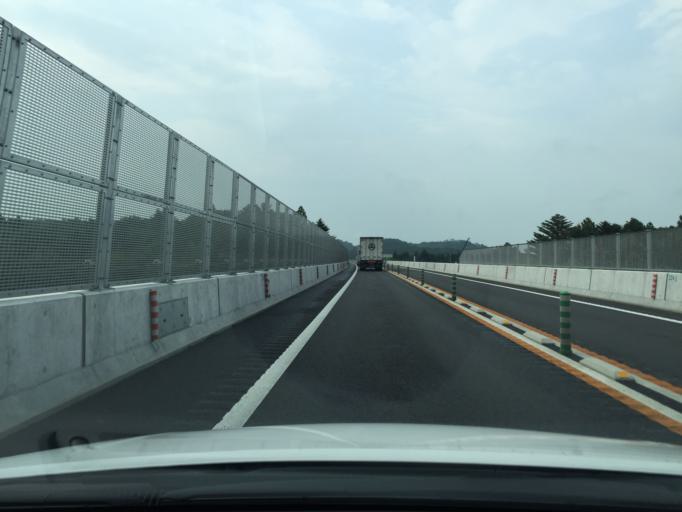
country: JP
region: Fukushima
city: Namie
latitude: 37.4257
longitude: 140.9618
